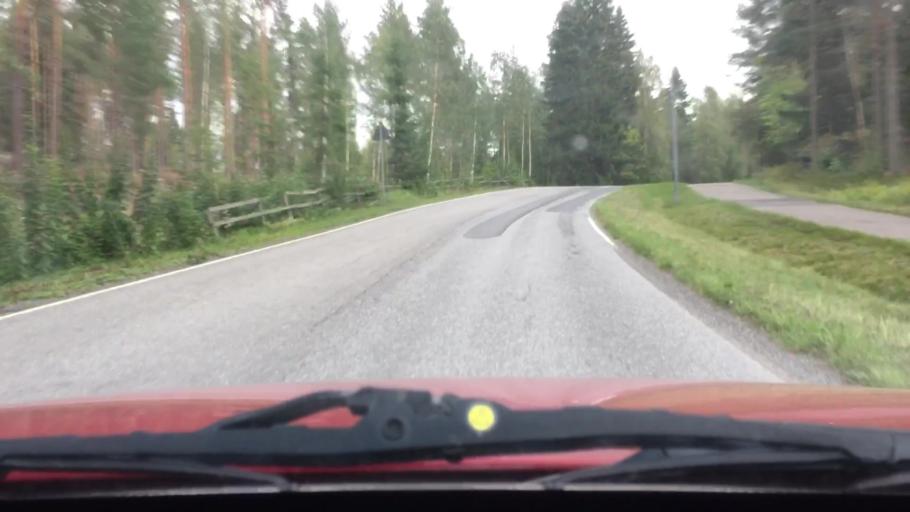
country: FI
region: Varsinais-Suomi
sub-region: Turku
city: Masku
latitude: 60.5548
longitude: 22.1307
